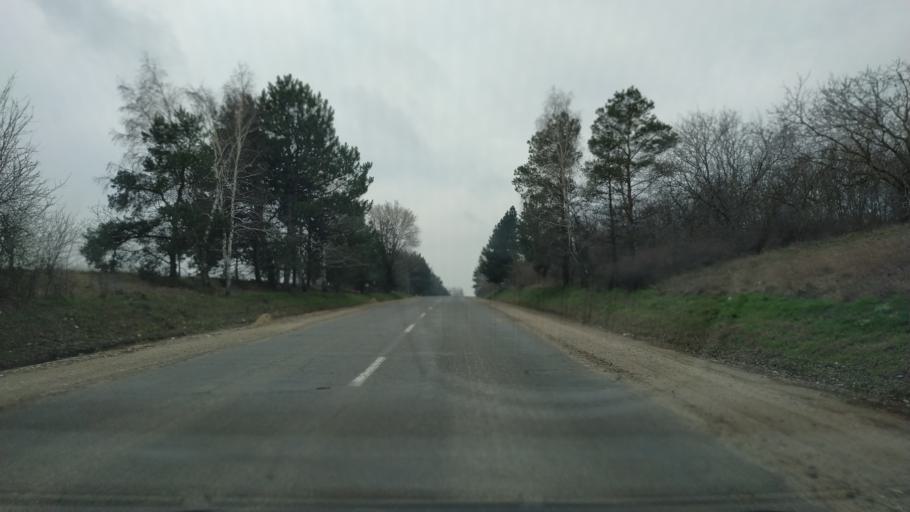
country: MD
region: Cahul
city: Cahul
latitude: 45.9389
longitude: 28.2892
